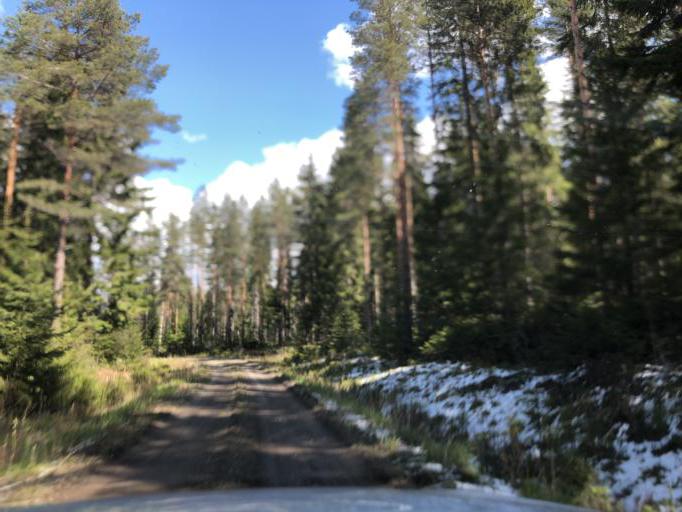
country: SE
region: Dalarna
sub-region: Avesta Kommun
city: Horndal
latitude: 60.2314
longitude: 16.6005
